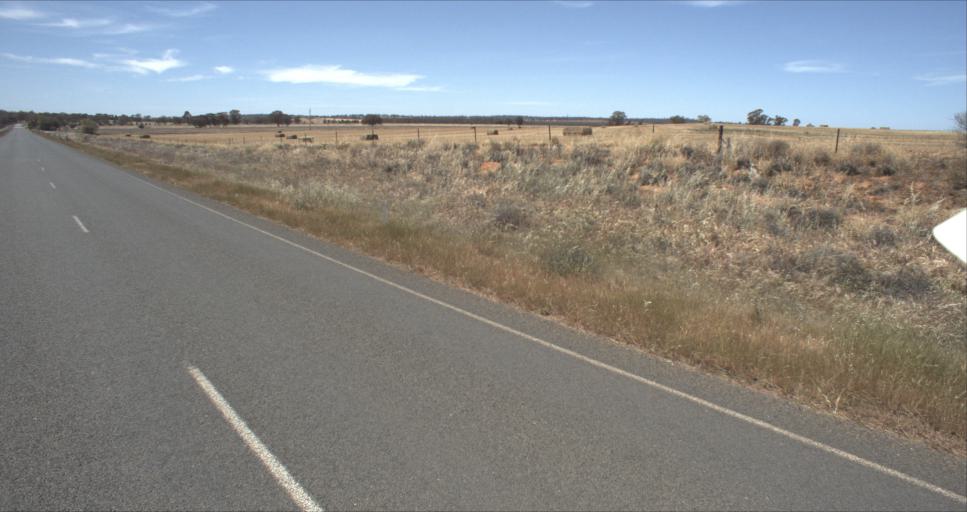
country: AU
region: New South Wales
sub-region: Leeton
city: Leeton
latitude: -34.6528
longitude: 146.4626
